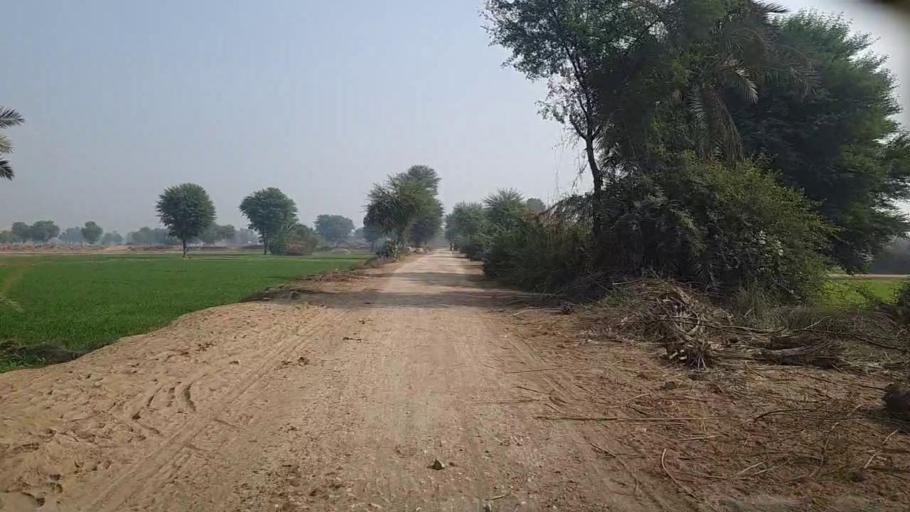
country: PK
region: Sindh
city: Setharja Old
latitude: 27.1413
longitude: 68.4953
